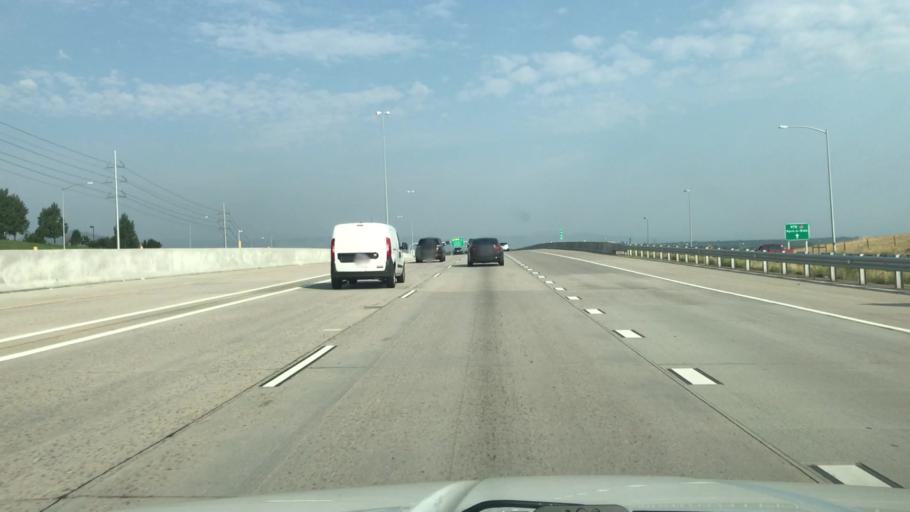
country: US
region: Colorado
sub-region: Broomfield County
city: Broomfield
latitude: 39.9295
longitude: -105.1172
